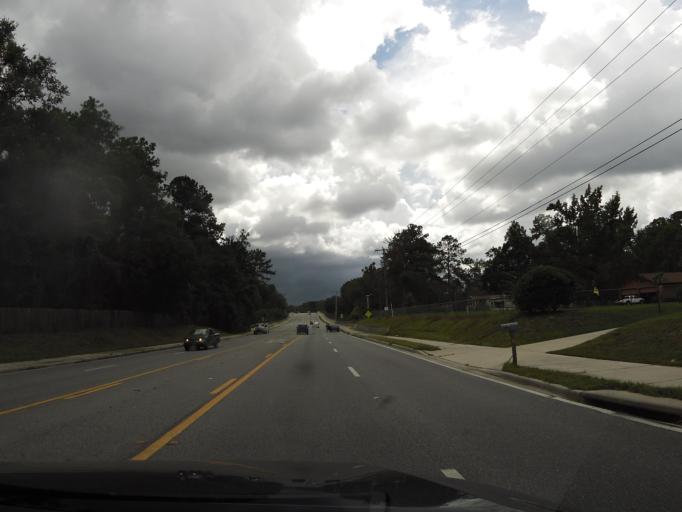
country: US
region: Florida
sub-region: Clay County
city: Asbury Lake
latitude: 30.0869
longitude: -81.8096
